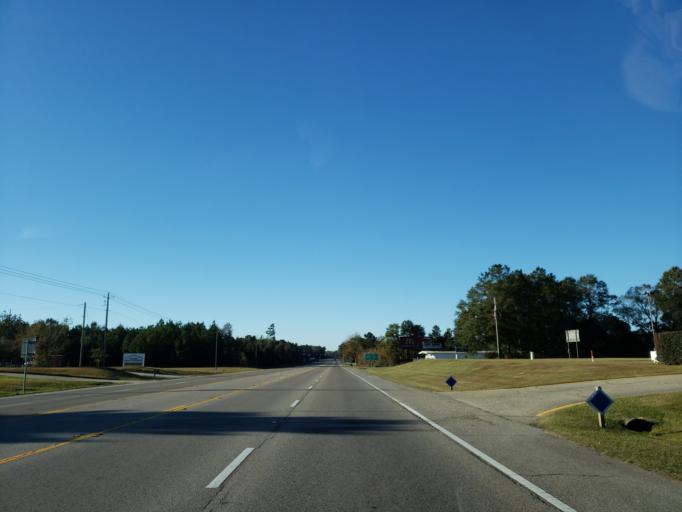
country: US
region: Mississippi
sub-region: Forrest County
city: Hattiesburg
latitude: 31.2822
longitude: -89.2944
